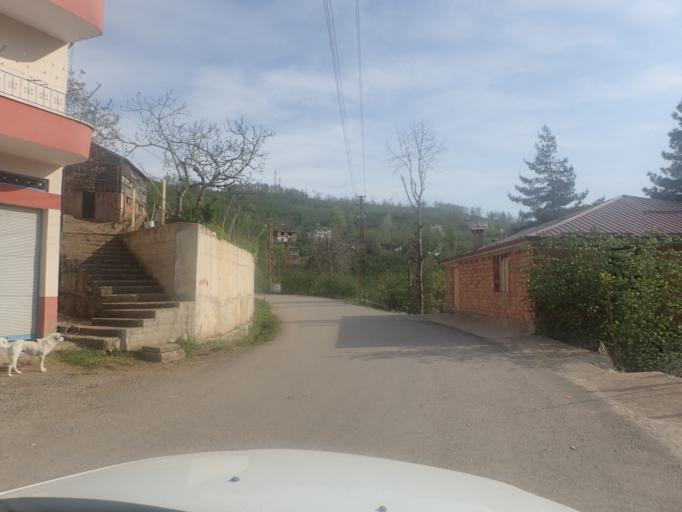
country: TR
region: Ordu
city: Catalpinar
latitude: 40.8805
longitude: 37.4827
